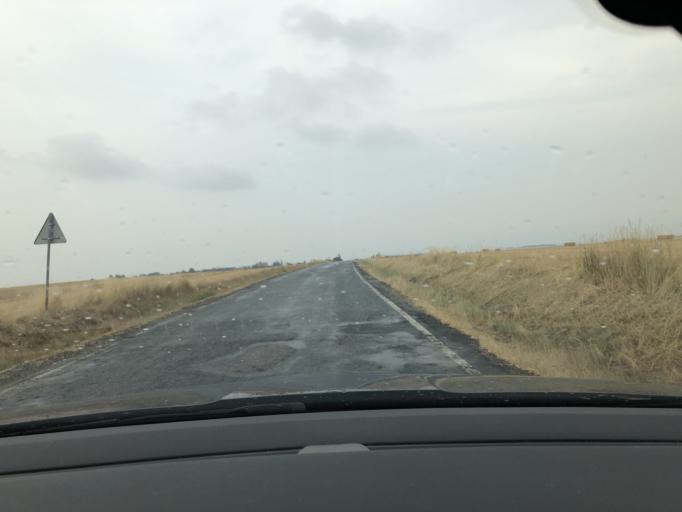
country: CZ
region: South Moravian
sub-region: Okres Znojmo
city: Jevisovice
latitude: 49.0274
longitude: 16.0395
